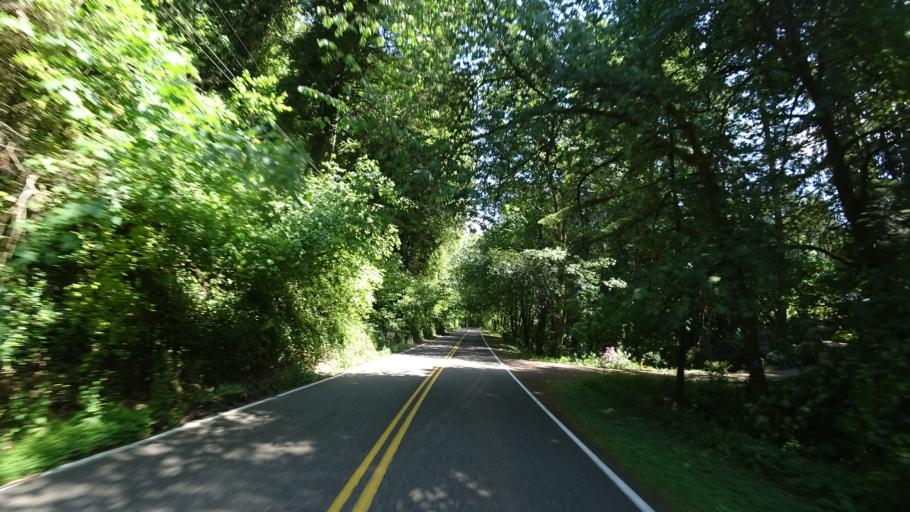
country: US
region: Oregon
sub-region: Clackamas County
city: Lake Oswego
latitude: 45.4465
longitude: -122.6971
